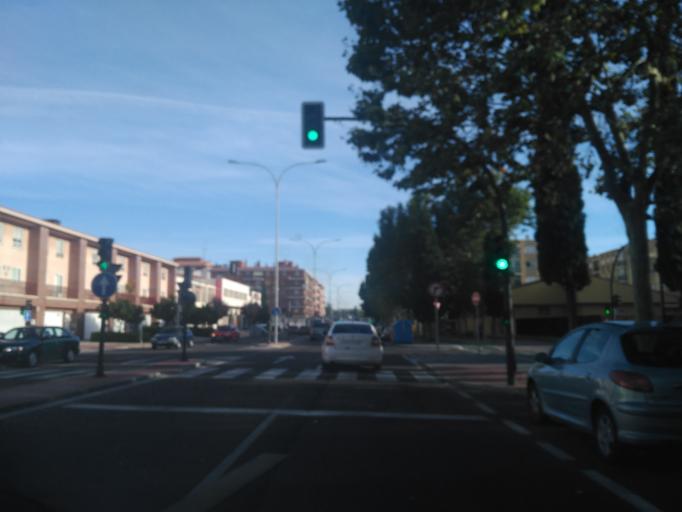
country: ES
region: Castille and Leon
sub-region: Provincia de Salamanca
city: Salamanca
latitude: 40.9757
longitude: -5.6484
